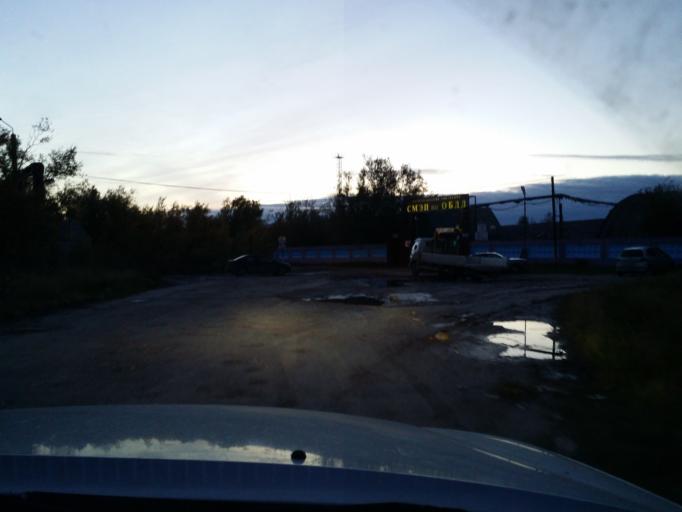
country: RU
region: Khanty-Mansiyskiy Avtonomnyy Okrug
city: Nizhnevartovsk
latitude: 60.9605
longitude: 76.5276
